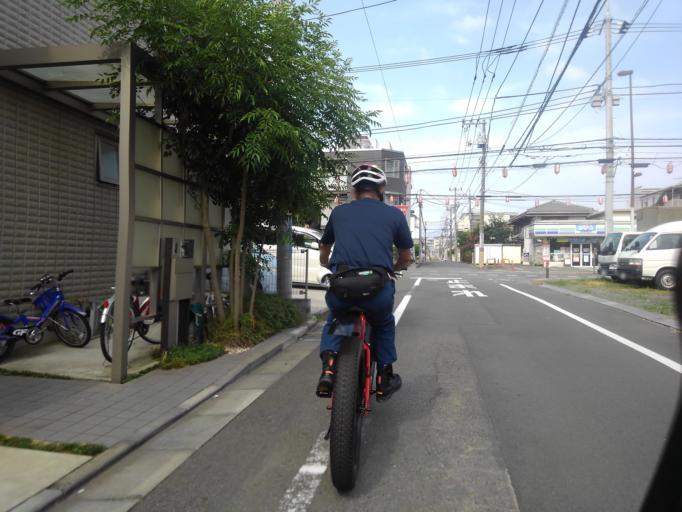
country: JP
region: Kanagawa
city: Minami-rinkan
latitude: 35.4739
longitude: 139.4626
